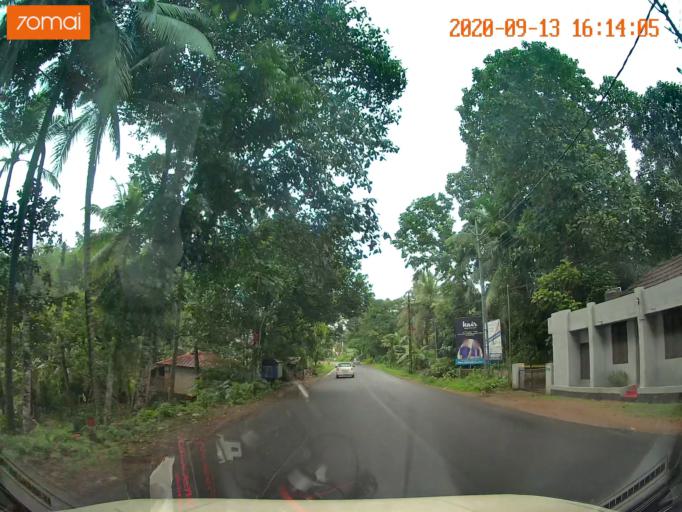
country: IN
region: Kerala
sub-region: Kottayam
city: Palackattumala
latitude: 9.6887
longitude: 76.6321
